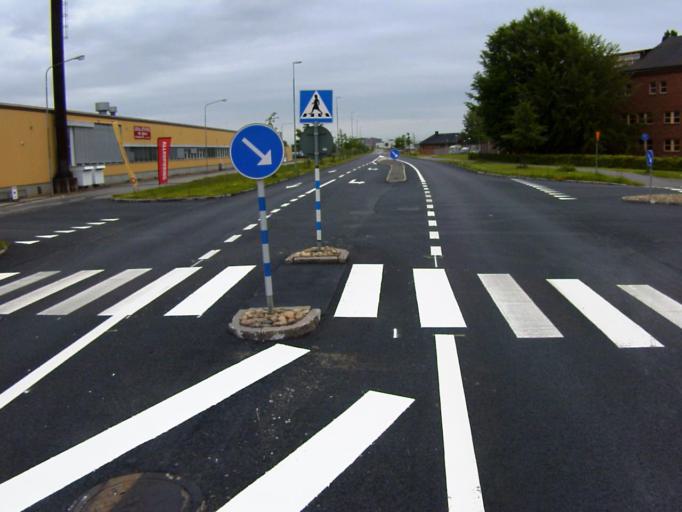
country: SE
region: Skane
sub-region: Kristianstads Kommun
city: Kristianstad
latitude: 56.0380
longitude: 14.1532
